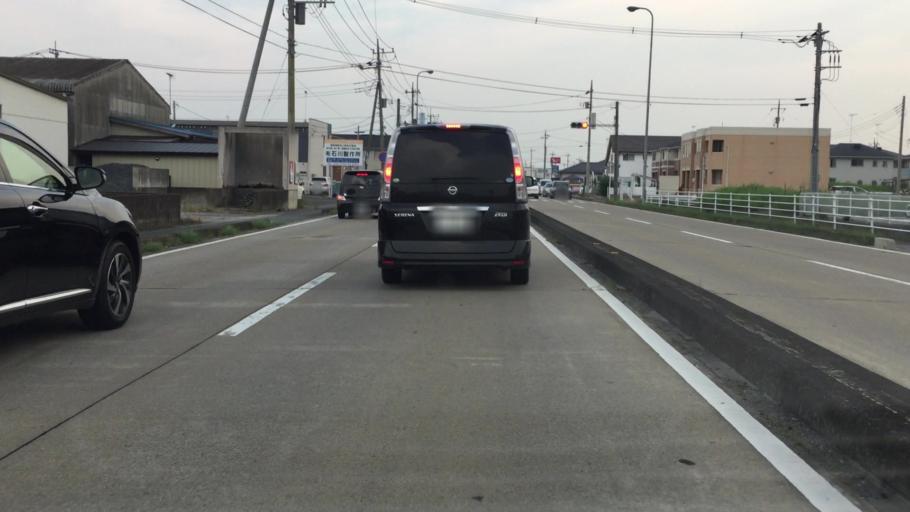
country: JP
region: Tochigi
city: Tochigi
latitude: 36.3457
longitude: 139.7017
